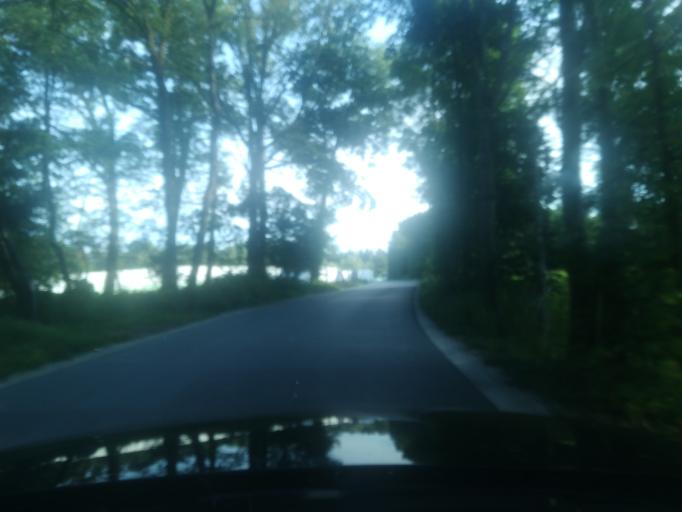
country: AT
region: Upper Austria
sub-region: Wels-Land
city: Marchtrenk
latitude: 48.1630
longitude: 14.1668
